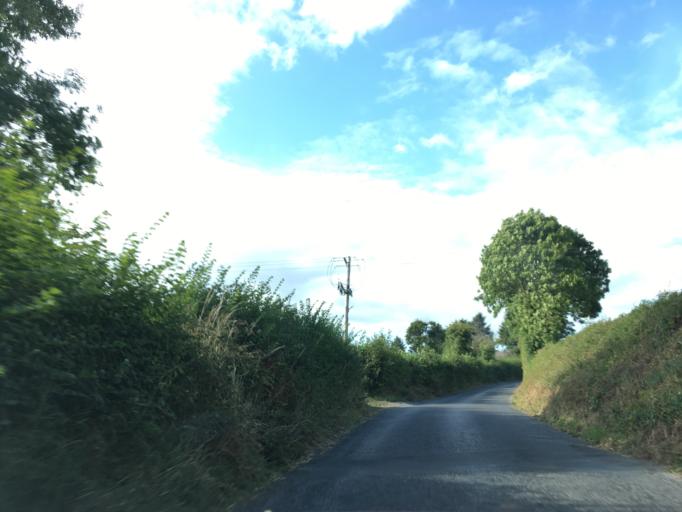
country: IE
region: Munster
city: Cahir
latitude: 52.2865
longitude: -7.9553
